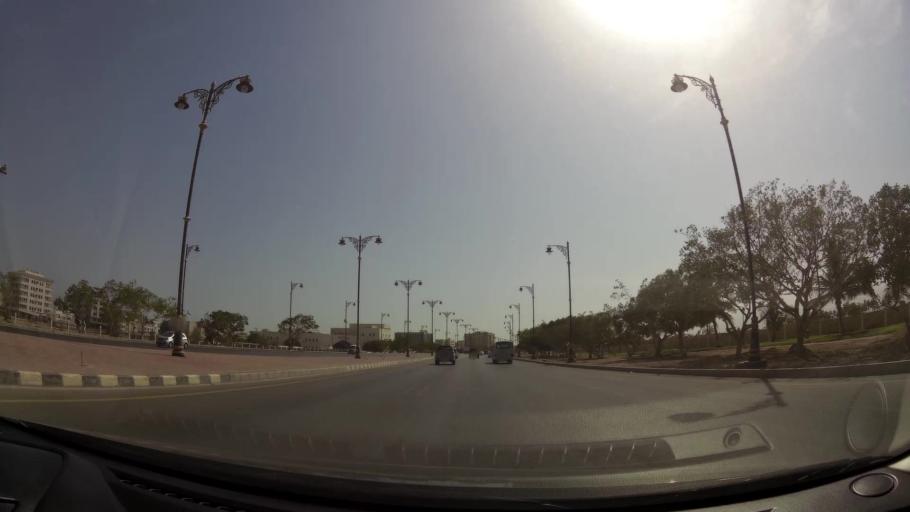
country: OM
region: Zufar
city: Salalah
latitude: 17.0242
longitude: 54.0887
